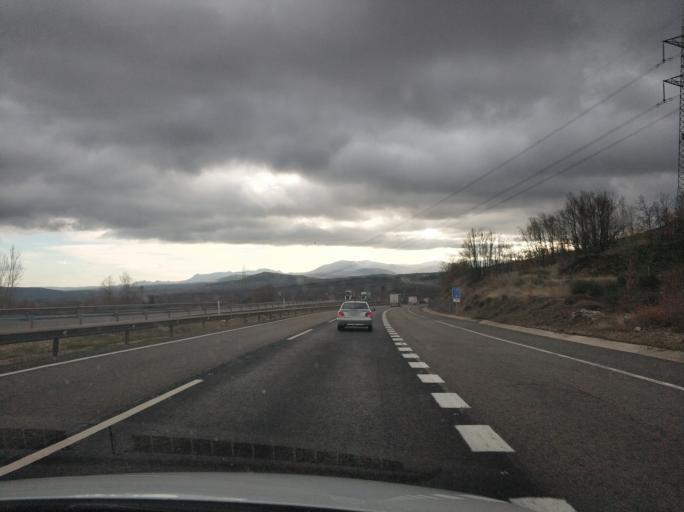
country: ES
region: Madrid
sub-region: Provincia de Madrid
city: Horcajo de la Sierra
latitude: 41.0840
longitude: -3.5970
